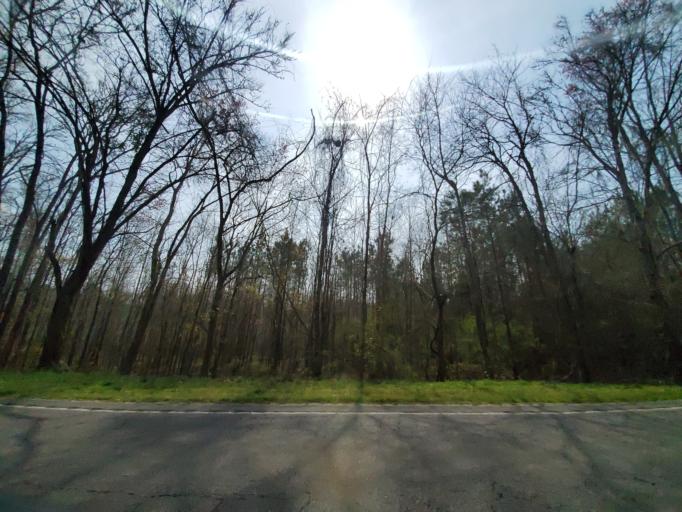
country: US
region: South Carolina
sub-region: Dorchester County
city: Ridgeville
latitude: 32.9676
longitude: -80.3003
